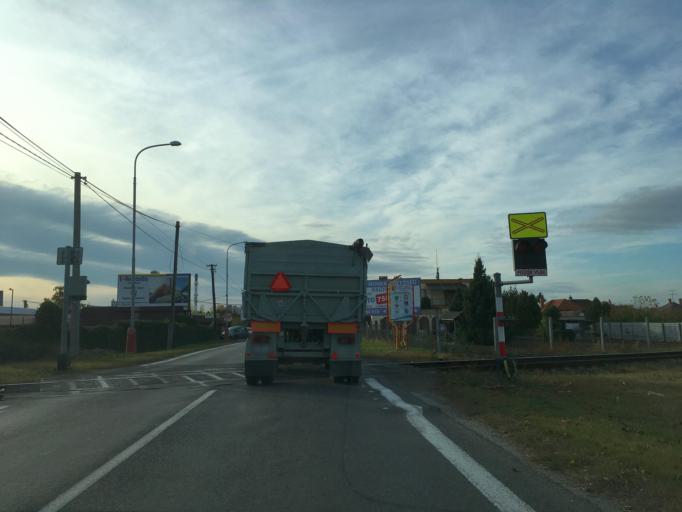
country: SK
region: Trnavsky
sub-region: Okres Dunajska Streda
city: Velky Meder
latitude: 47.8548
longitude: 17.7867
